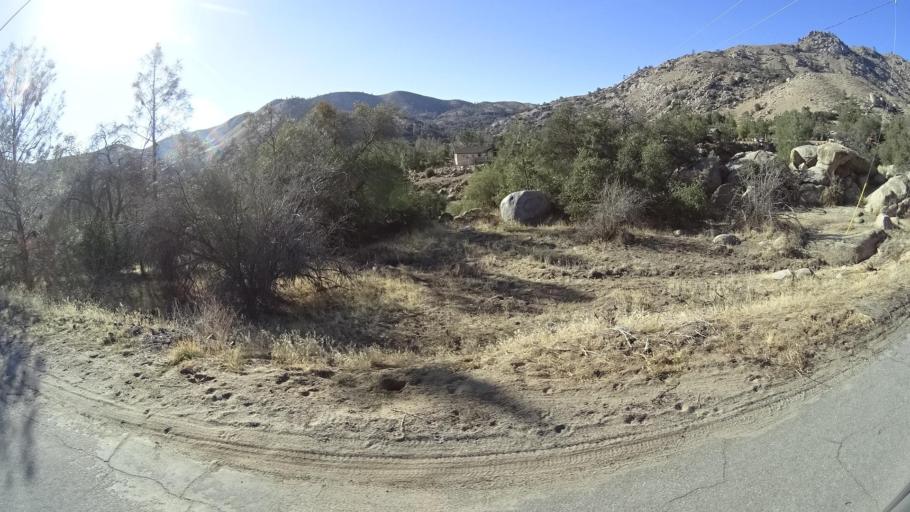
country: US
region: California
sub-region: Kern County
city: Weldon
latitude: 35.7117
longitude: -118.3049
